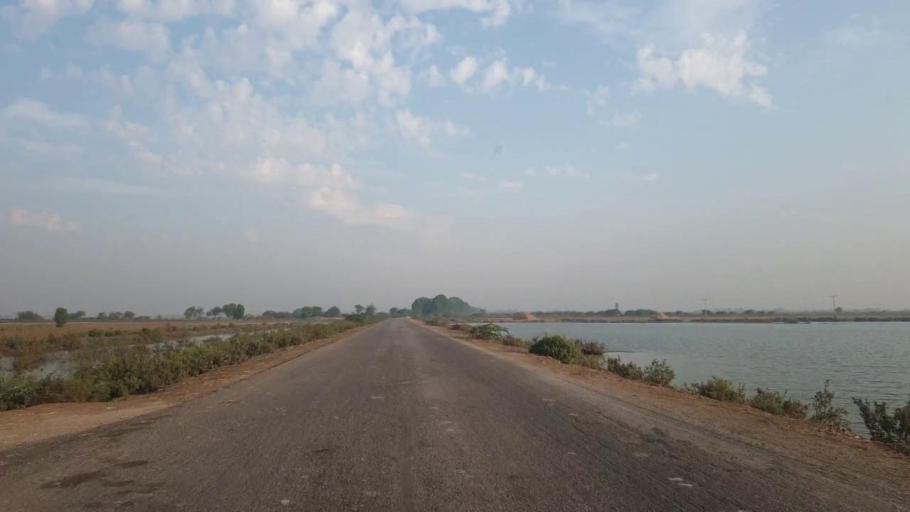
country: PK
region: Sindh
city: Tando Bago
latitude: 24.7231
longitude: 68.9423
